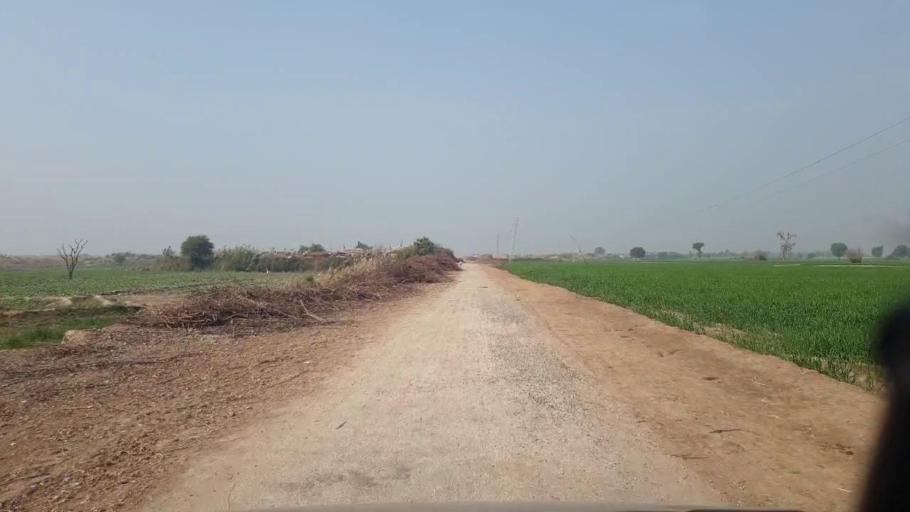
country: PK
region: Sindh
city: Shahdadpur
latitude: 26.0312
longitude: 68.5271
